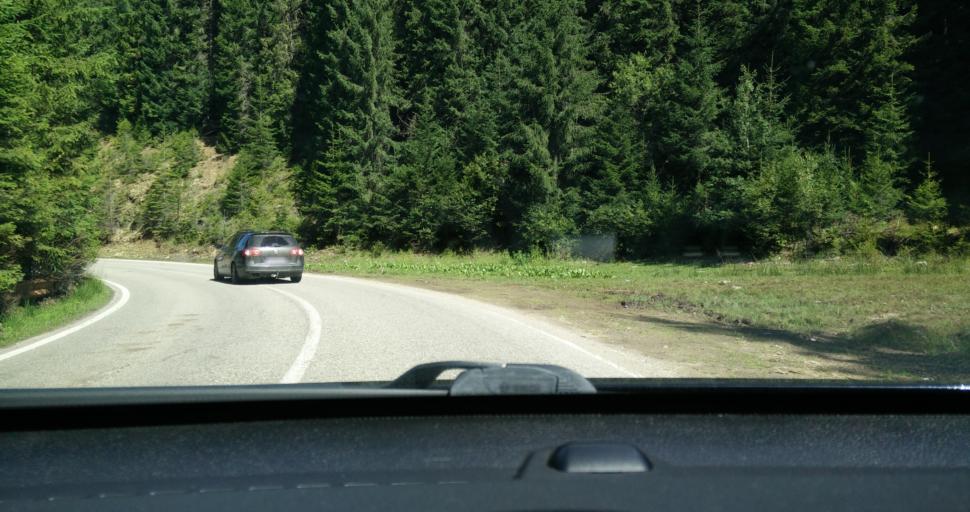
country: RO
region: Alba
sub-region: Comuna Sugag
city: Sugag
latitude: 45.5446
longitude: 23.6376
